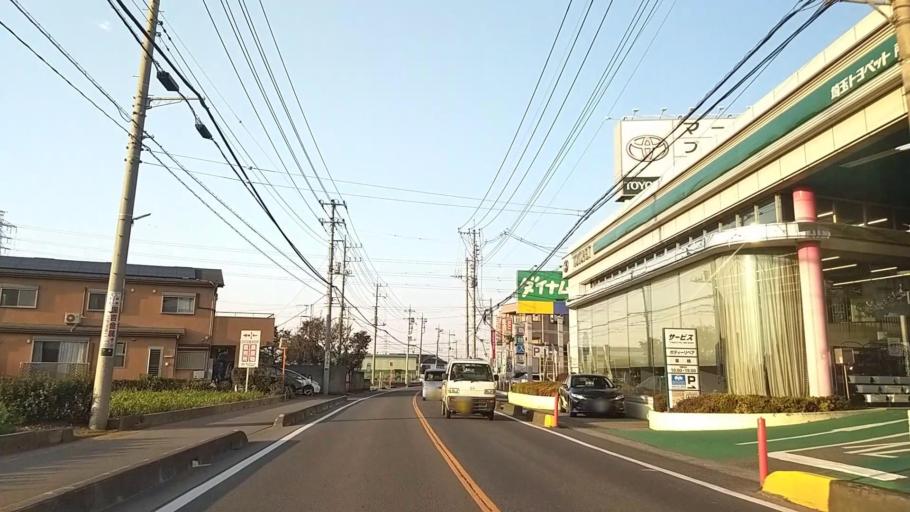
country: JP
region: Saitama
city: Tokorozawa
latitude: 35.8318
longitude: 139.4649
